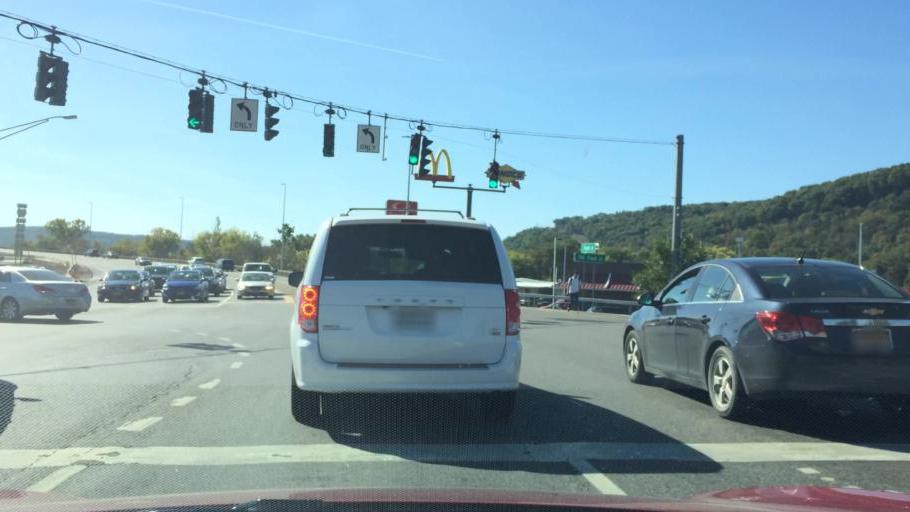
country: US
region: New York
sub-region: Broome County
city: Port Dickinson
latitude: 42.1273
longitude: -75.9044
